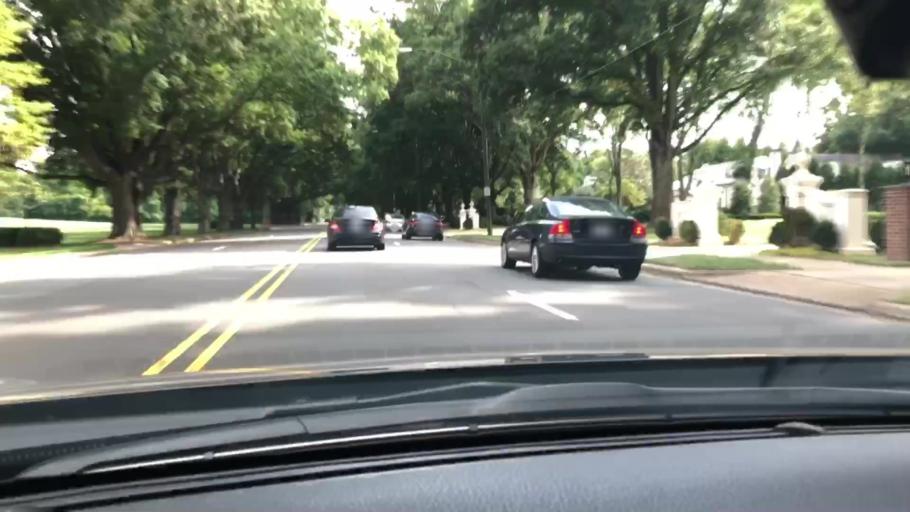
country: US
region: North Carolina
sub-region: Mecklenburg County
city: Charlotte
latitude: 35.1647
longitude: -80.8213
